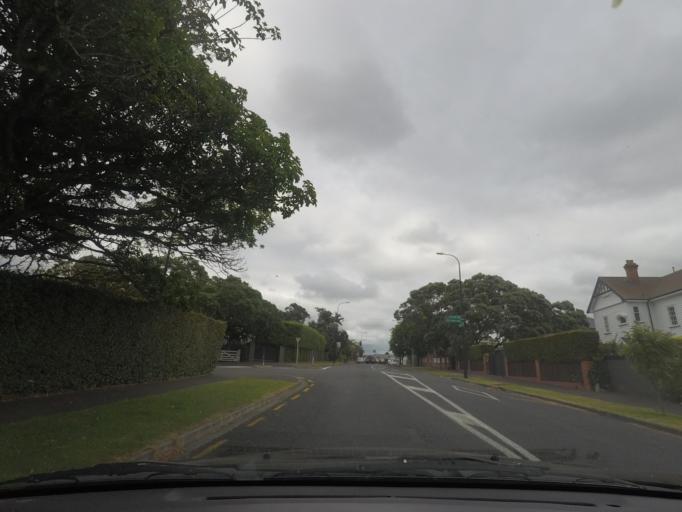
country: NZ
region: Auckland
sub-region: Auckland
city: Auckland
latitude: -36.8735
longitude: 174.7854
